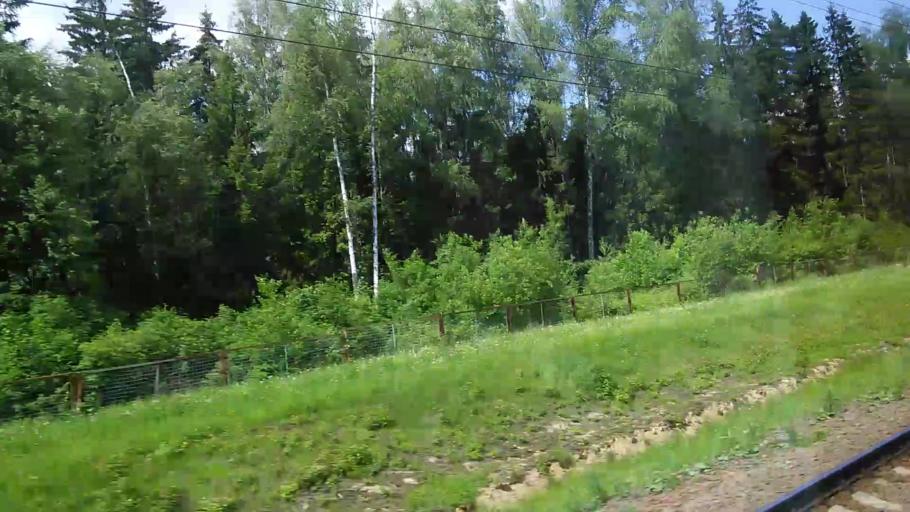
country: RU
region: Moskovskaya
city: Lobnya
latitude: 55.9890
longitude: 37.4703
